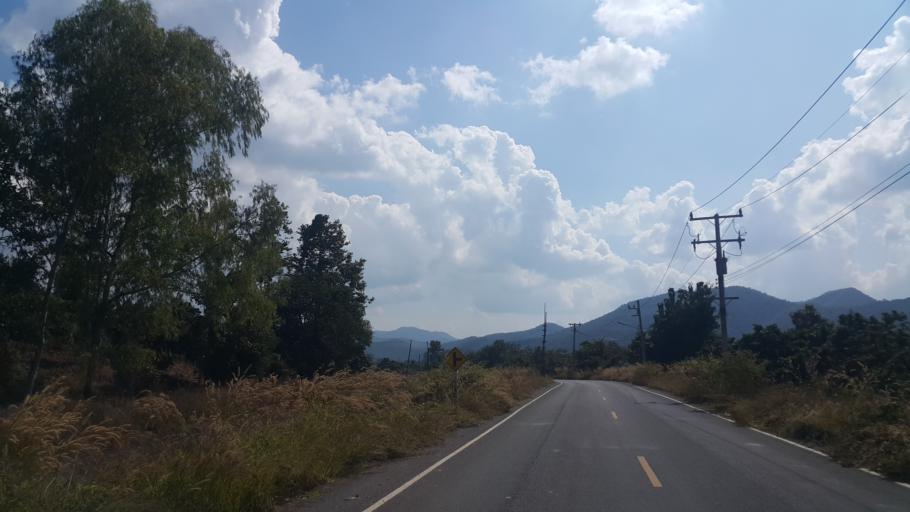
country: TH
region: Lamphun
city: Ban Thi
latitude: 18.6306
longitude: 99.1595
